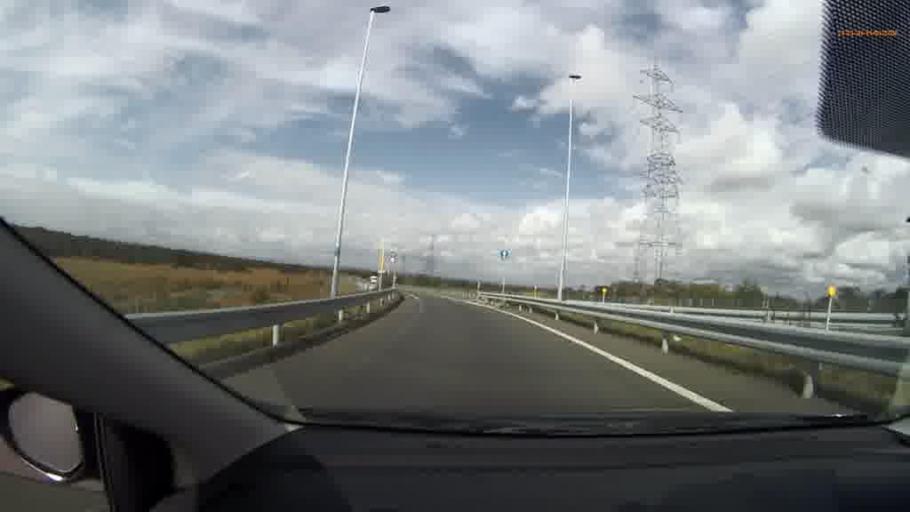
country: JP
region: Hokkaido
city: Kushiro
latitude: 43.0303
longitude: 144.4013
